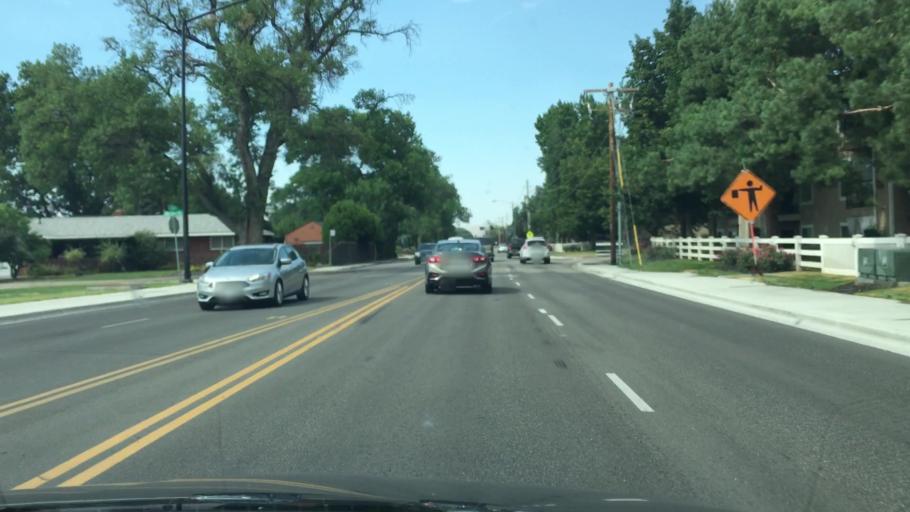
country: US
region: Idaho
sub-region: Ada County
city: Garden City
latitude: 43.6212
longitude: -116.2742
